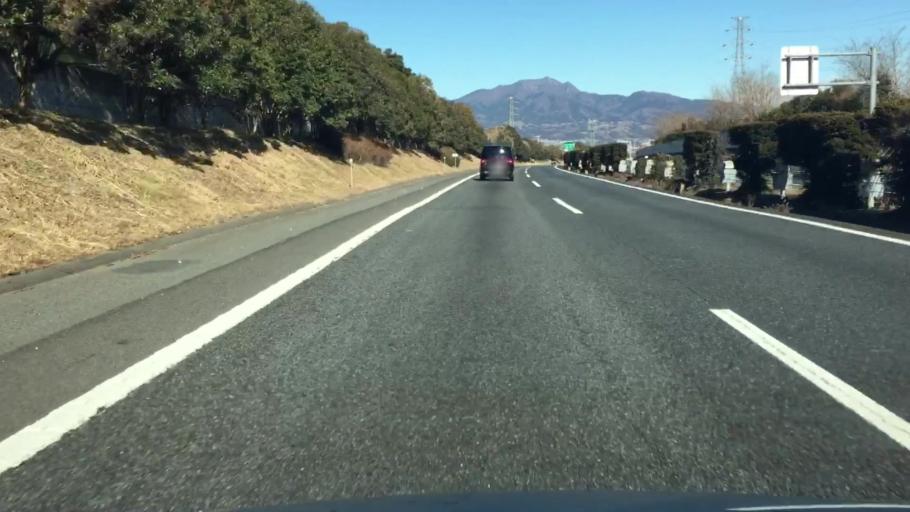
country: JP
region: Gunma
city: Shibukawa
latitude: 36.4620
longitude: 139.0117
